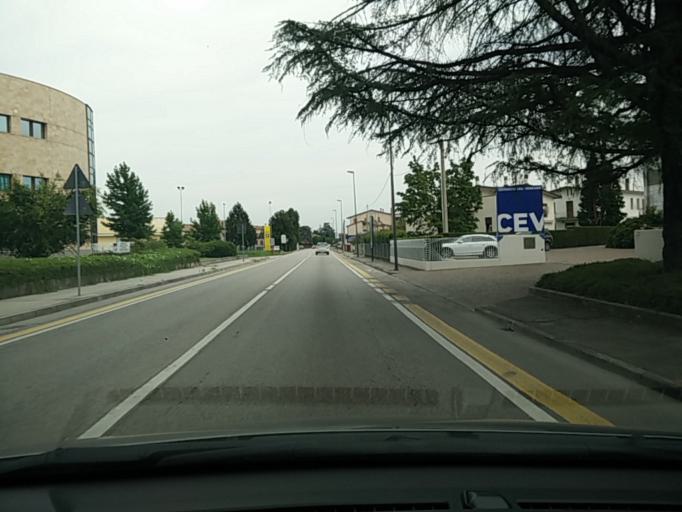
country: IT
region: Veneto
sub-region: Provincia di Treviso
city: Treviso
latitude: 45.6699
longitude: 12.2067
